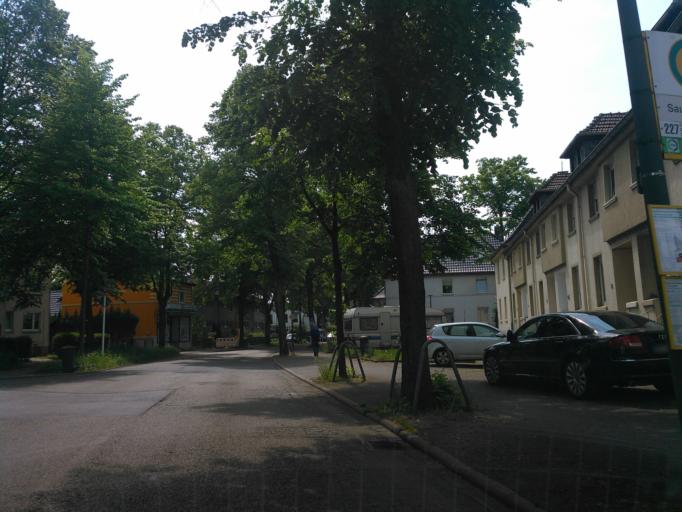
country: DE
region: North Rhine-Westphalia
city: Marl
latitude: 51.6604
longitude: 7.0777
